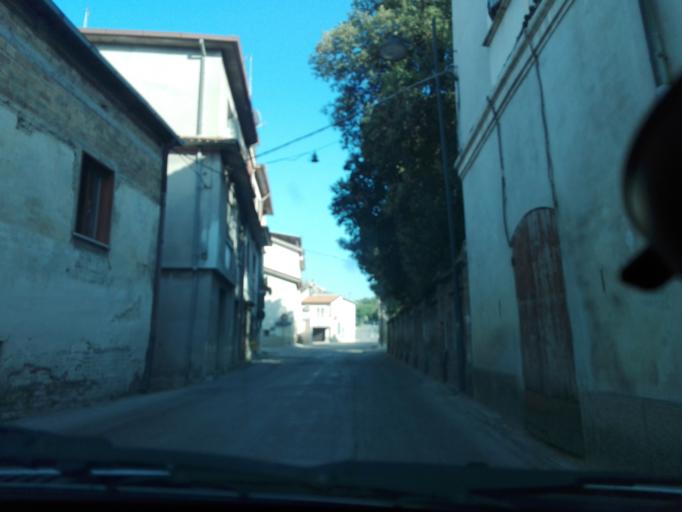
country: IT
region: Abruzzo
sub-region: Provincia di Pescara
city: Cappelle sul Tavo
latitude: 42.4633
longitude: 14.1043
